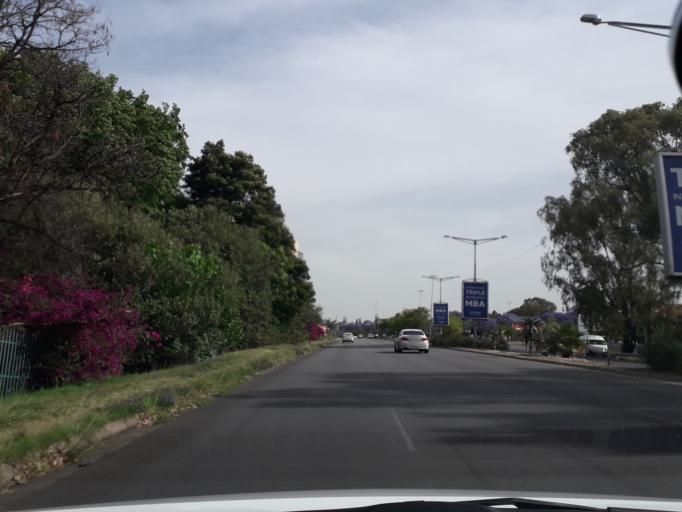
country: ZA
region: Gauteng
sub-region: City of Johannesburg Metropolitan Municipality
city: Johannesburg
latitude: -26.1222
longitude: 28.0323
